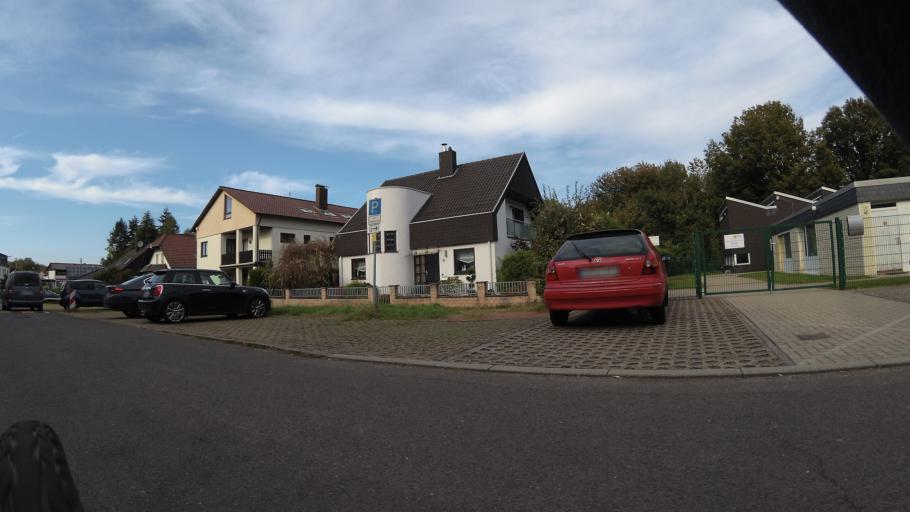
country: DE
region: Saarland
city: Friedrichsthal
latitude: 49.3296
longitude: 7.0899
